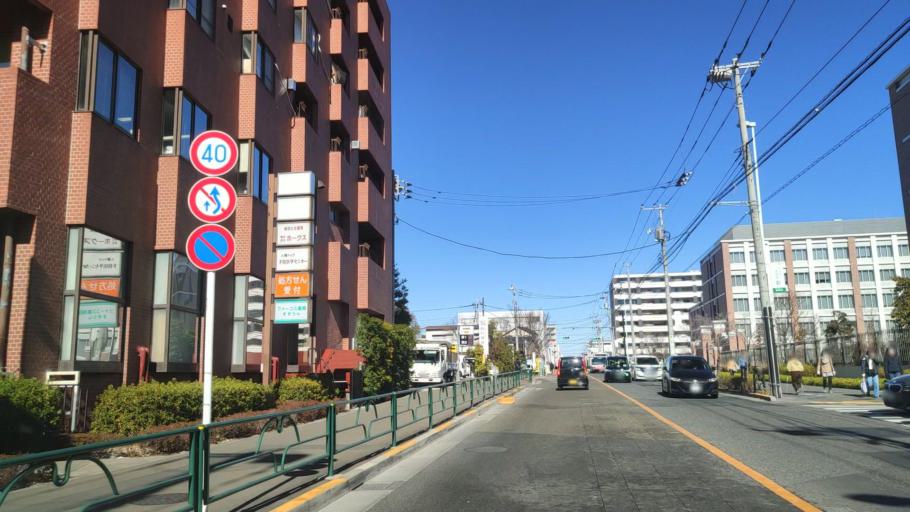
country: JP
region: Tokyo
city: Mitaka-shi
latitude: 35.6845
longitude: 139.5684
